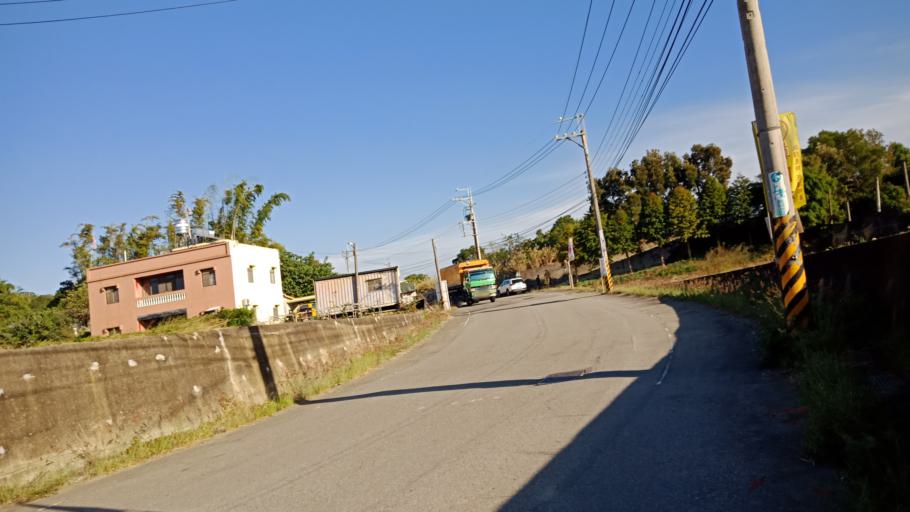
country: TW
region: Taiwan
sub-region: Miaoli
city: Miaoli
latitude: 24.4842
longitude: 120.7033
